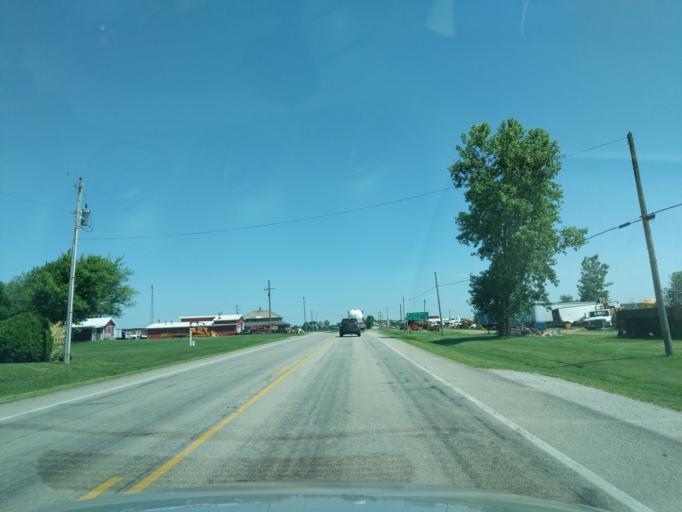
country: US
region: Indiana
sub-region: Whitley County
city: Columbia City
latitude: 41.0758
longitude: -85.4702
